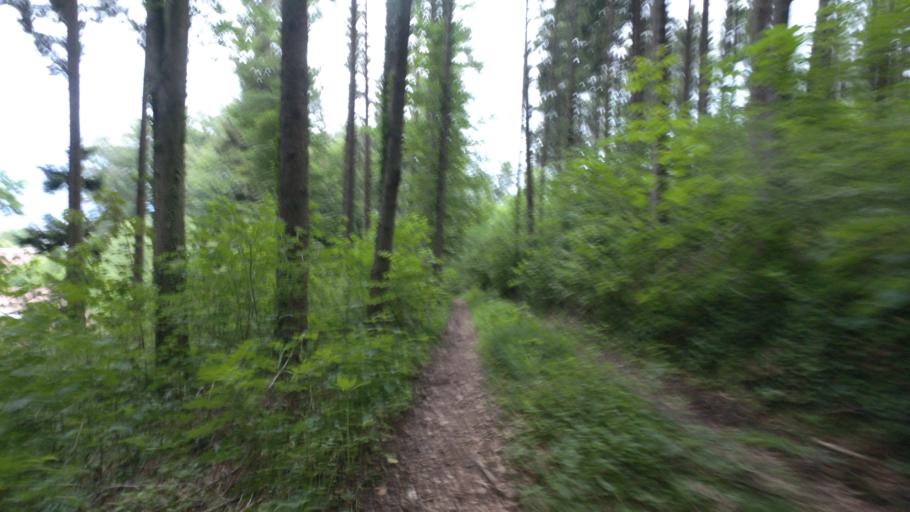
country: DE
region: Bavaria
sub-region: Upper Bavaria
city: Chieming
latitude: 47.9287
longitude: 12.5552
